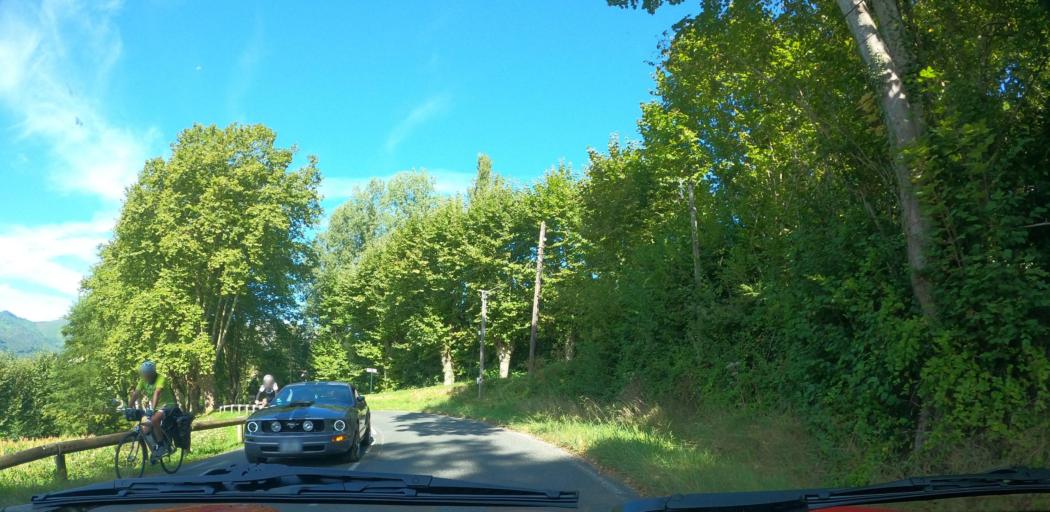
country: FR
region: Aquitaine
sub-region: Departement des Pyrenees-Atlantiques
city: Sare
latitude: 43.3098
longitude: -1.5707
